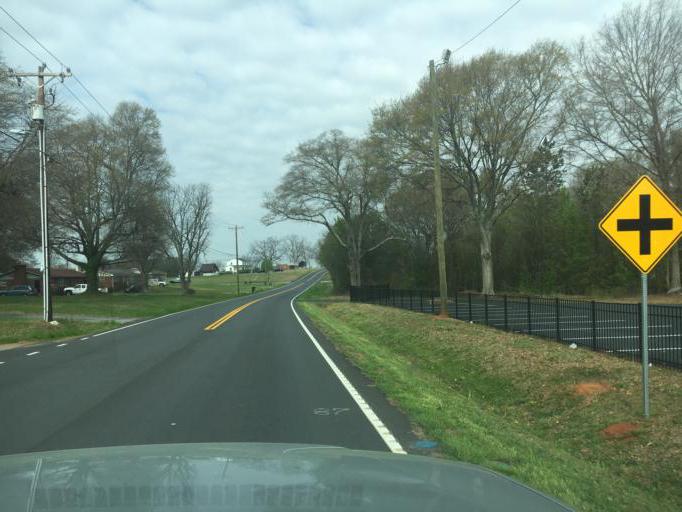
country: US
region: South Carolina
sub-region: Spartanburg County
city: Inman Mills
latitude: 35.0307
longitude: -82.1230
